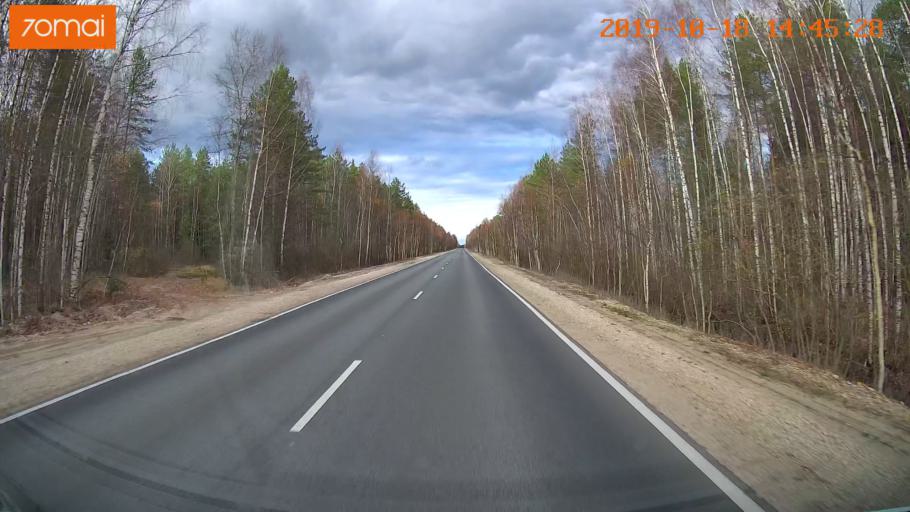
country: RU
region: Vladimir
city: Velikodvorskiy
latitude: 55.3553
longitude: 40.6789
